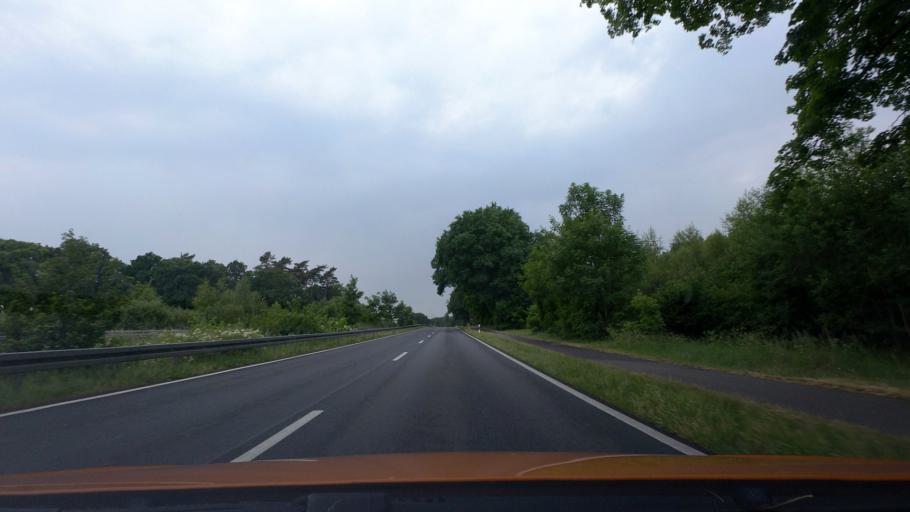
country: DE
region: Lower Saxony
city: Linsburg
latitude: 52.5519
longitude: 9.3478
